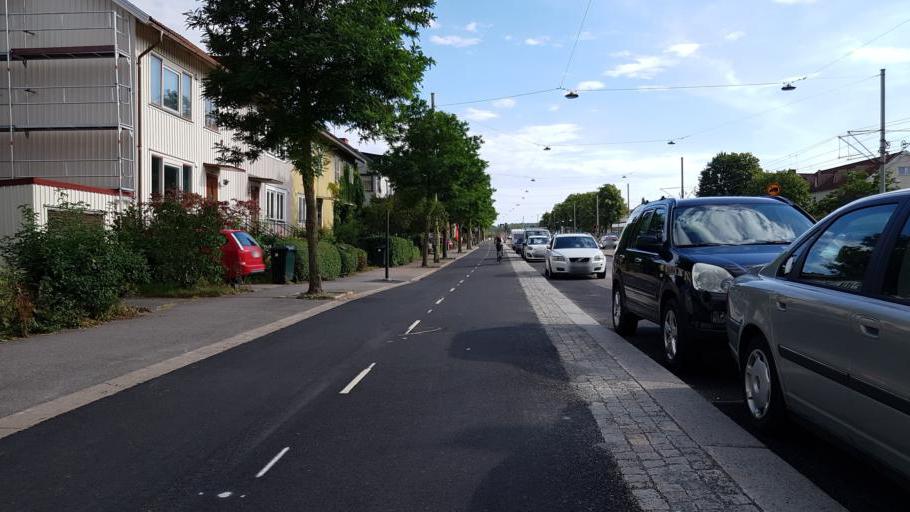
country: SE
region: Vaestra Goetaland
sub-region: Goteborg
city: Goeteborg
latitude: 57.7148
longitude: 12.0250
